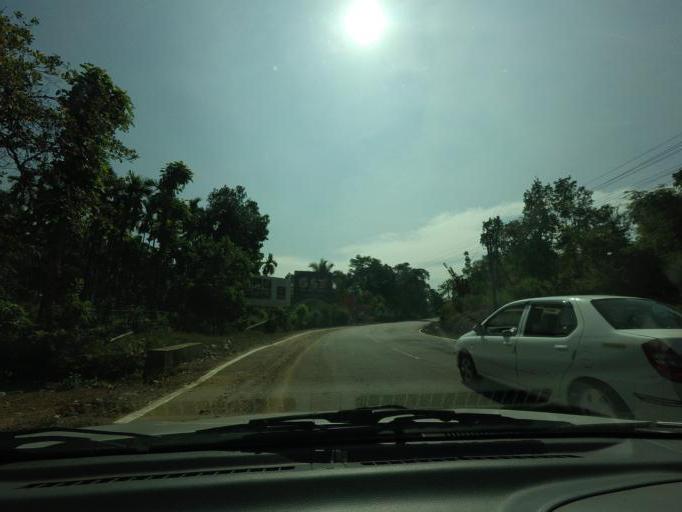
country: IN
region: Karnataka
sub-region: Dakshina Kannada
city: Sulya
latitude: 12.6815
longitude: 75.6100
